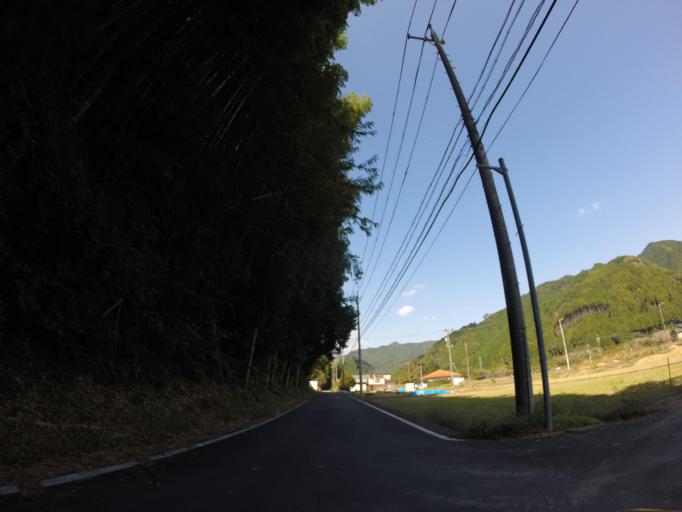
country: JP
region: Shizuoka
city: Shizuoka-shi
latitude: 35.1134
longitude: 138.4595
